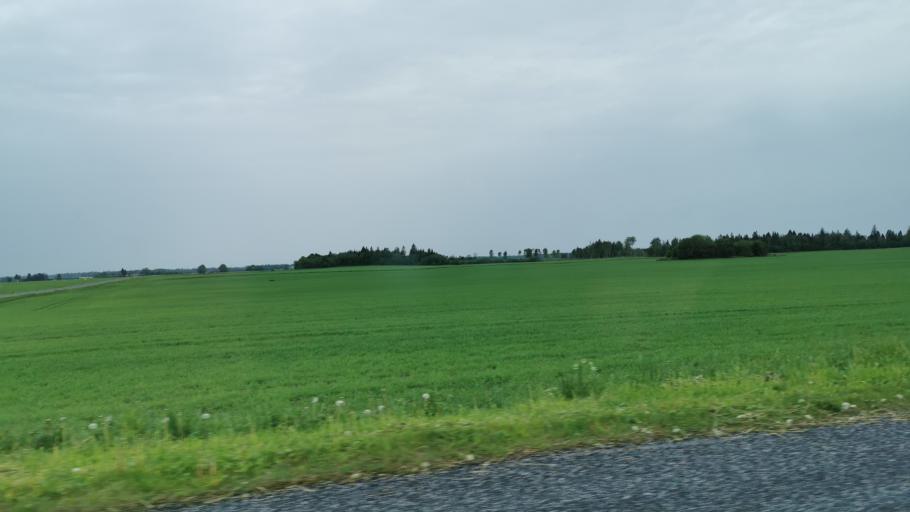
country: EE
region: Laeaene-Virumaa
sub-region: Vaeike-Maarja vald
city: Vaike-Maarja
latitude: 59.1621
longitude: 26.2944
